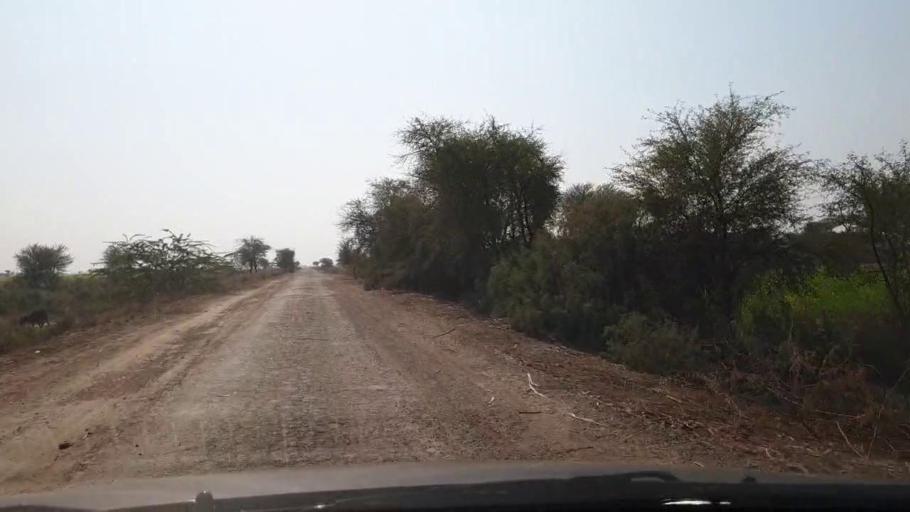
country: PK
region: Sindh
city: Jhol
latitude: 25.8807
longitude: 68.9972
